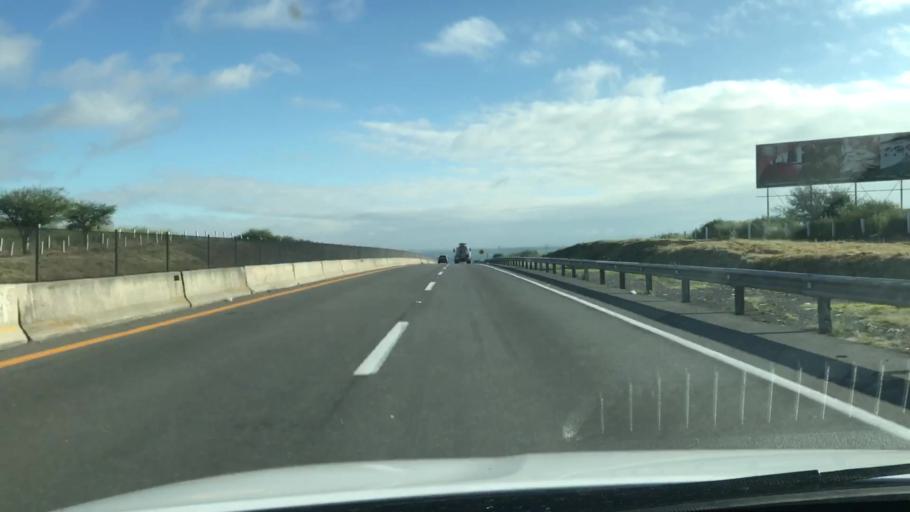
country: MX
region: Jalisco
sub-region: San Juan de los Lagos
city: Mezquitic de la Magdalena
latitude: 21.2126
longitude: -102.3248
